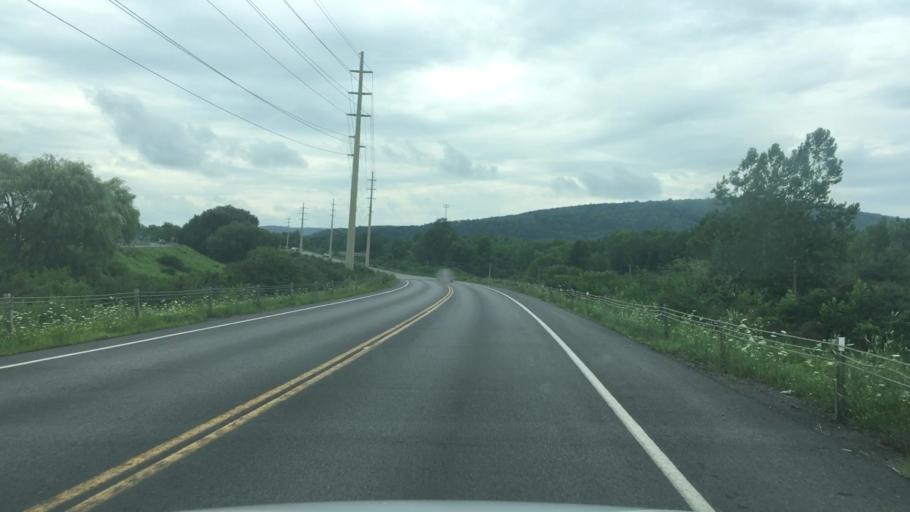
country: US
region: New York
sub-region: Otsego County
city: West End
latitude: 42.4440
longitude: -75.0998
